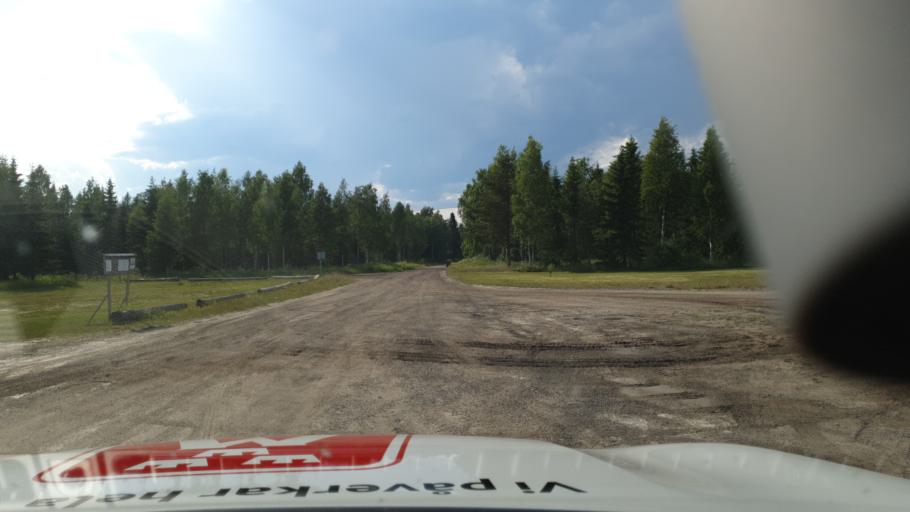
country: SE
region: Vaesterbotten
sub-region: Robertsfors Kommun
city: Robertsfors
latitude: 64.2169
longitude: 21.0785
